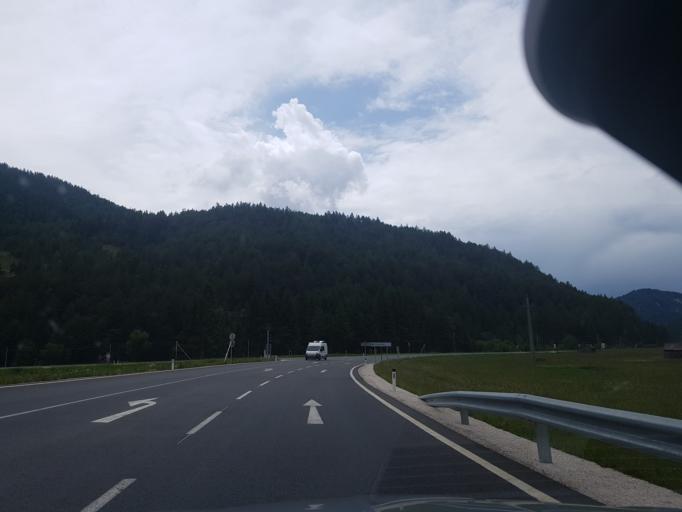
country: AT
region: Tyrol
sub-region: Politischer Bezirk Innsbruck Land
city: Scharnitz
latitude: 47.3861
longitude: 11.2521
